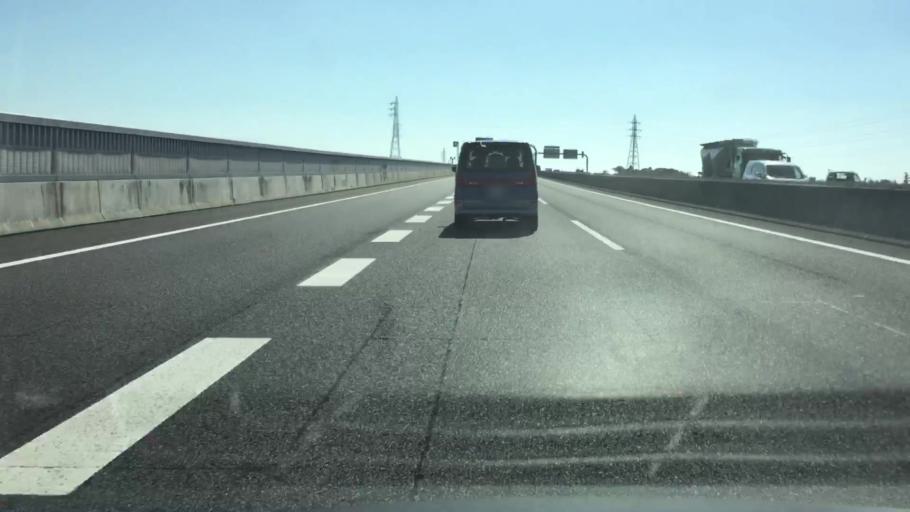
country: JP
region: Ibaraki
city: Naka
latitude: 36.0288
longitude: 140.1296
